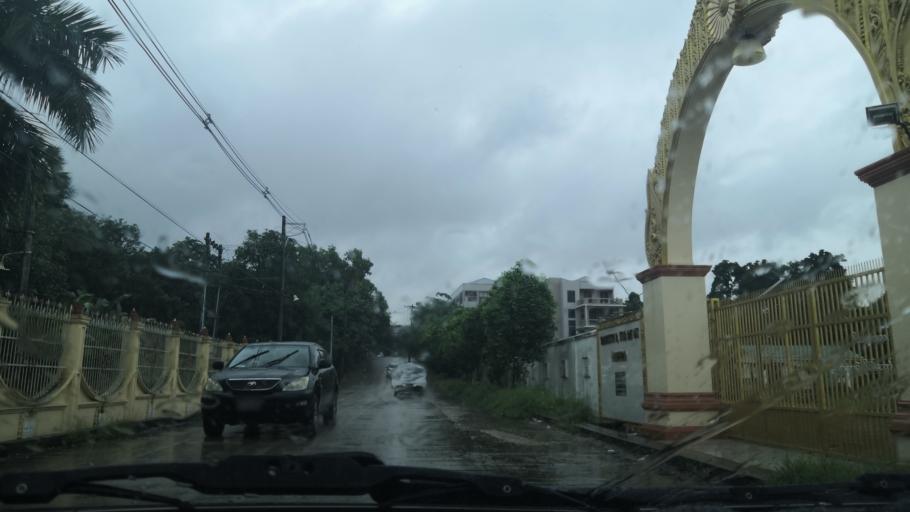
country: MM
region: Yangon
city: Yangon
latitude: 16.8853
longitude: 96.1499
